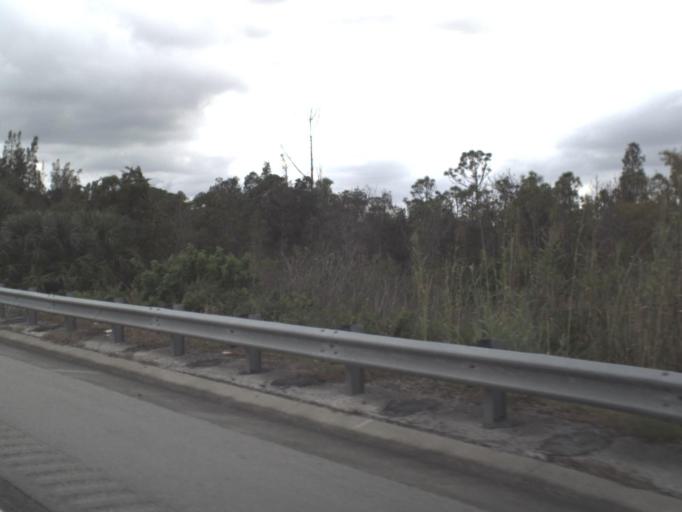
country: US
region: Florida
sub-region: Palm Beach County
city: Schall Circle
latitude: 26.7540
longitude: -80.1343
